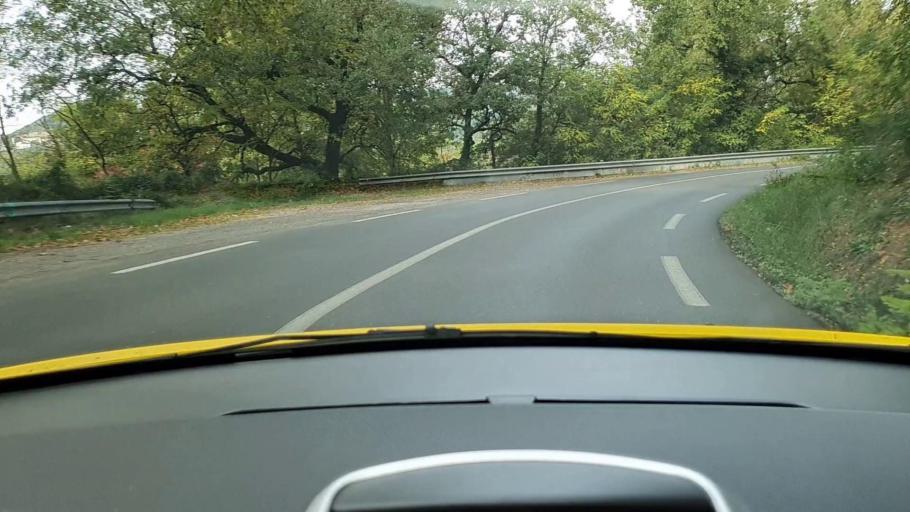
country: FR
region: Languedoc-Roussillon
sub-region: Departement du Gard
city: Aveze
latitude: 43.9757
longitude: 3.5902
